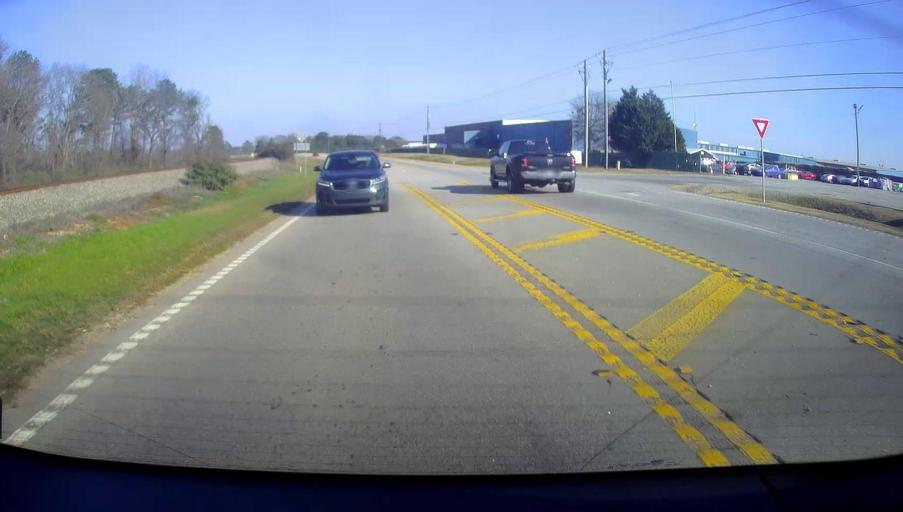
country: US
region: Georgia
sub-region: Butts County
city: Jackson
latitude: 33.3232
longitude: -84.0231
